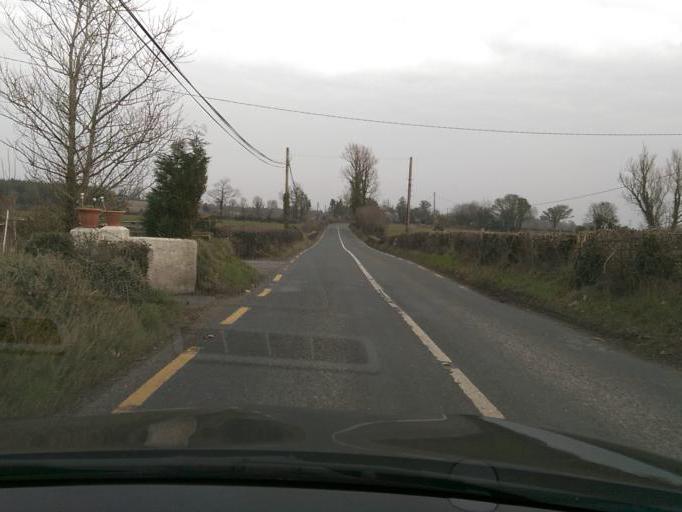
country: IE
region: Connaught
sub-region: Roscommon
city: Roscommon
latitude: 53.5124
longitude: -8.4049
